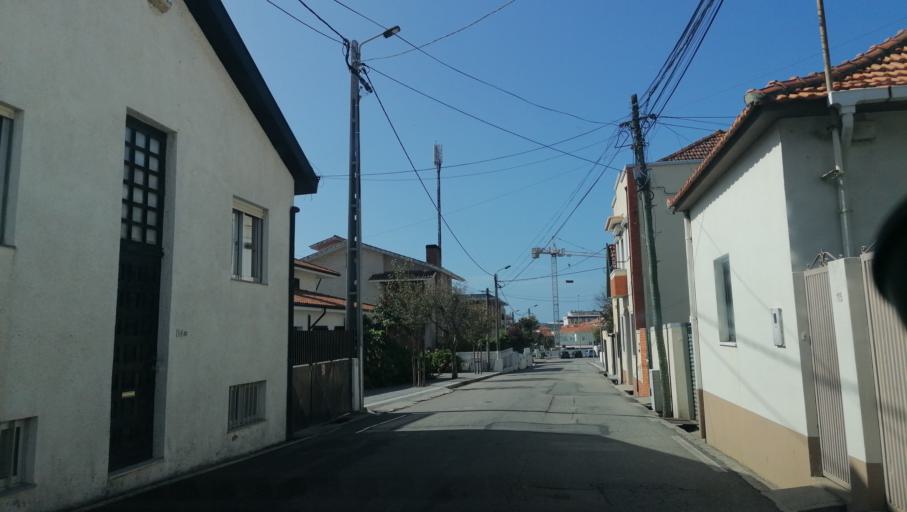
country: PT
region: Aveiro
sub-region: Espinho
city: Espinho
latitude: 41.0073
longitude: -8.6324
